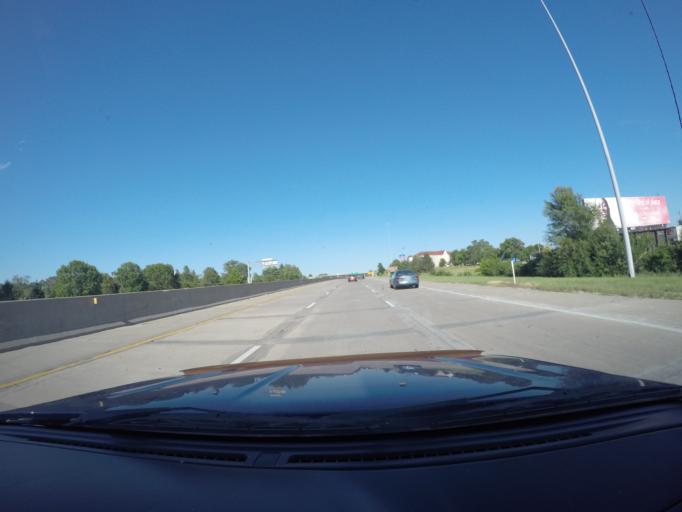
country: US
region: Kansas
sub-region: Shawnee County
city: Topeka
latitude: 39.0535
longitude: -95.7668
